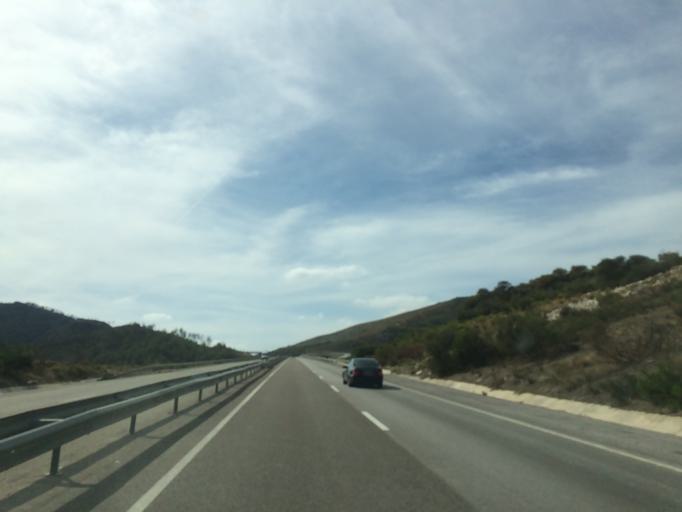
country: MA
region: Tanger-Tetouan
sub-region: Tanger-Assilah
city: Tangier
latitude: 35.7972
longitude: -5.5854
